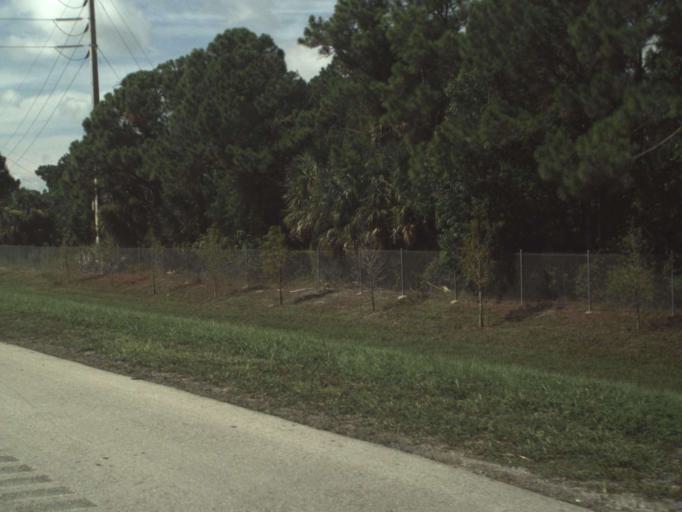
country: US
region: Florida
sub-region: Palm Beach County
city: Palm Beach Gardens
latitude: 26.8564
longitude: -80.1130
